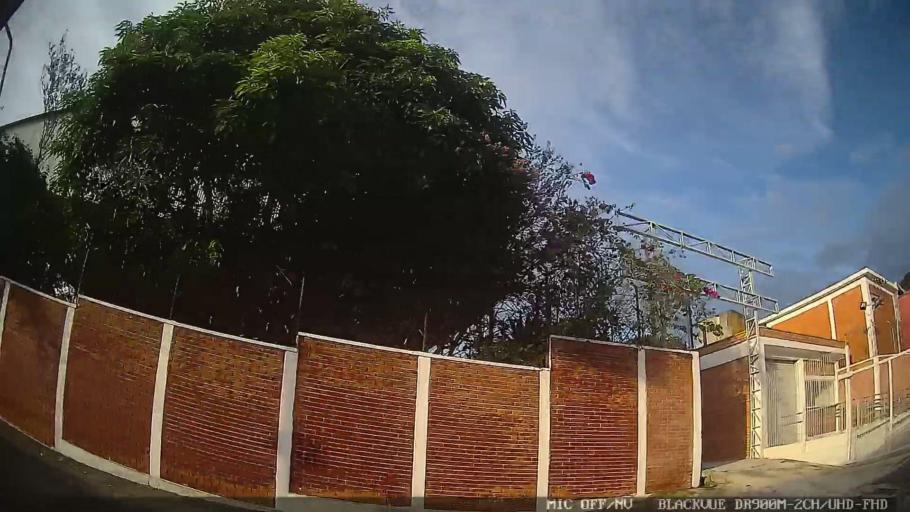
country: BR
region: Sao Paulo
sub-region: Mogi das Cruzes
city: Mogi das Cruzes
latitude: -23.5253
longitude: -46.1843
